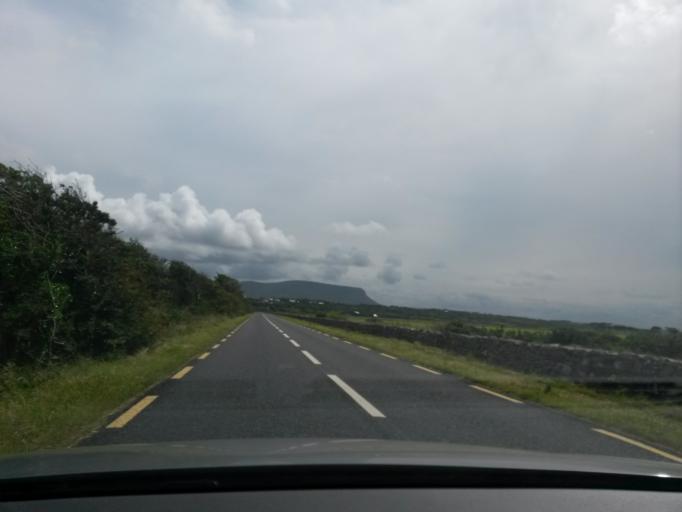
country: IE
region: Connaught
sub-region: County Leitrim
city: Kinlough
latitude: 54.4424
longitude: -8.4550
